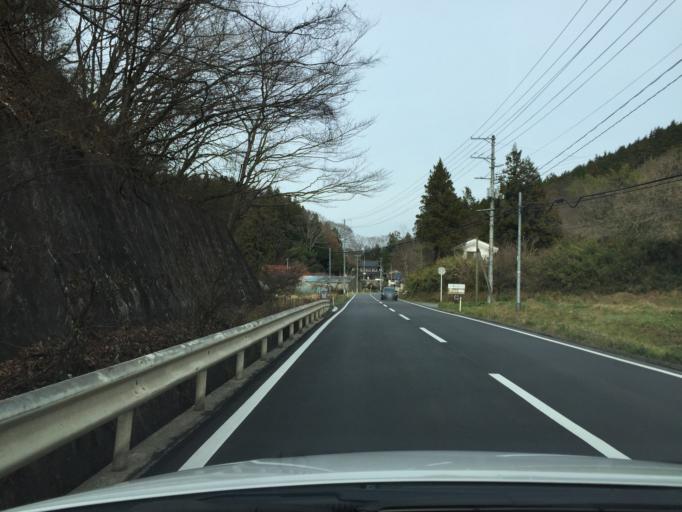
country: JP
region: Fukushima
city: Ishikawa
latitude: 37.2359
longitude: 140.6284
